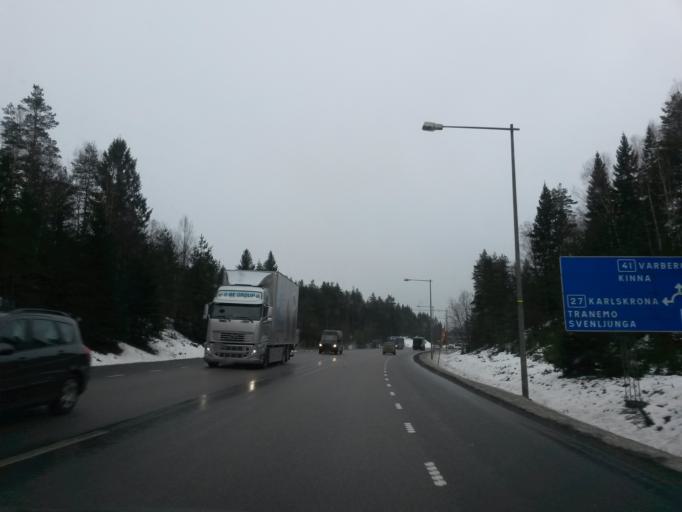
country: SE
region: Vaestra Goetaland
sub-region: Boras Kommun
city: Boras
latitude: 57.6857
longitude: 12.9411
